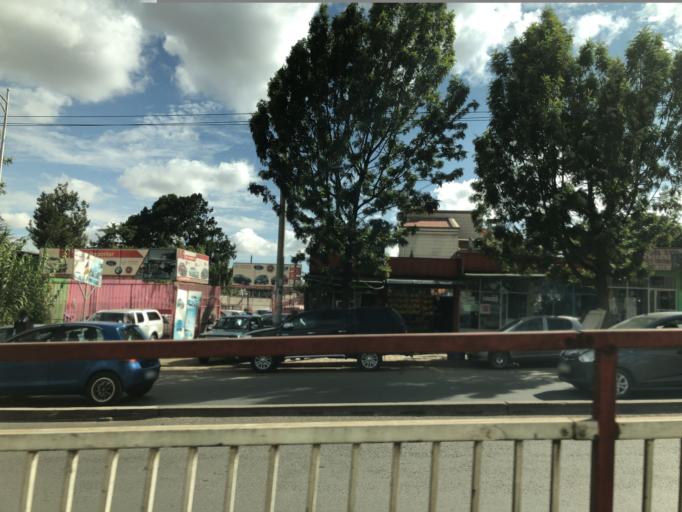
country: ET
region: Adis Abeba
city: Addis Ababa
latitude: 9.0234
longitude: 38.7787
